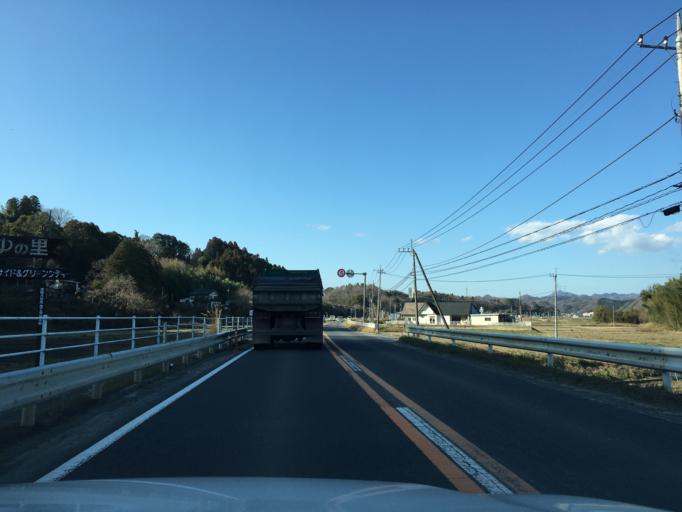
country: JP
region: Ibaraki
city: Omiya
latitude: 36.6061
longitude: 140.3988
